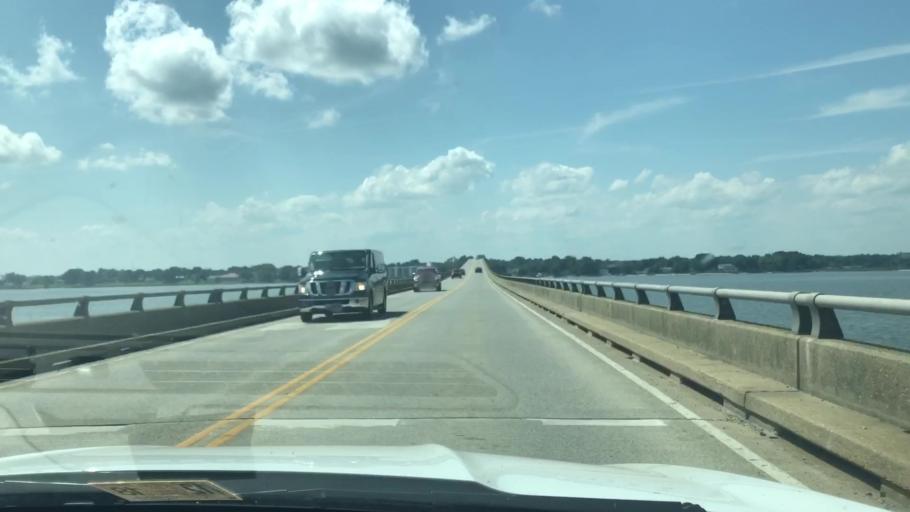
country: US
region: Virginia
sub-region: Essex County
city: Tappahannock
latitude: 37.9375
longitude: -76.8458
